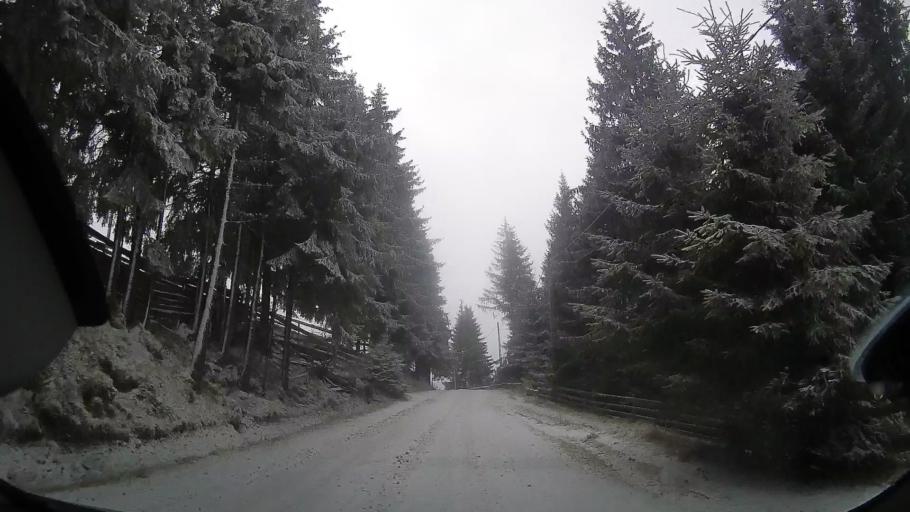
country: RO
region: Cluj
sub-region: Comuna Marisel
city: Marisel
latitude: 46.6586
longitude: 23.1408
